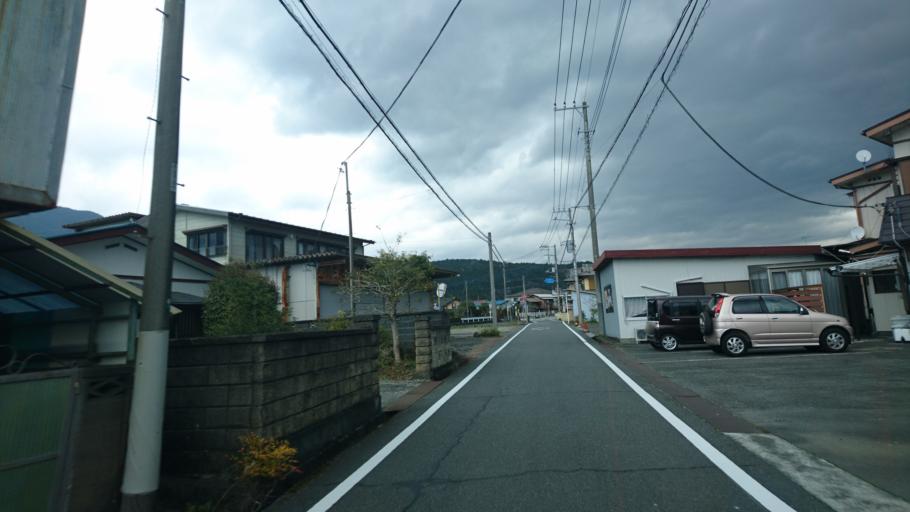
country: JP
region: Shizuoka
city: Fujinomiya
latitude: 35.2852
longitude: 138.5770
